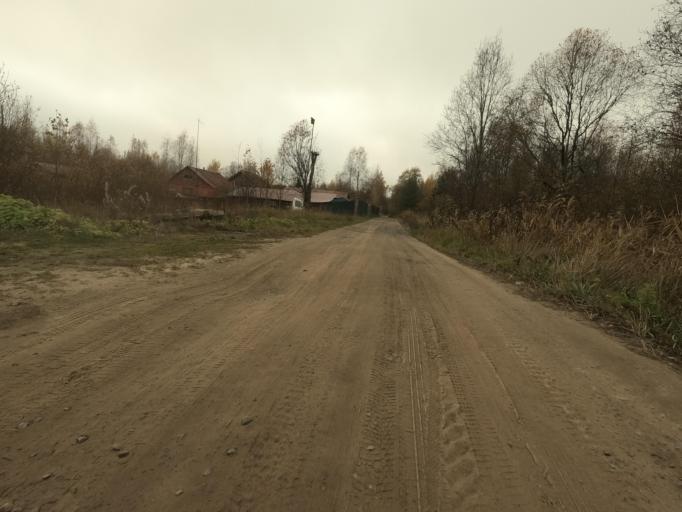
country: RU
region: Leningrad
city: Pavlovo
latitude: 59.7891
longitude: 30.8836
